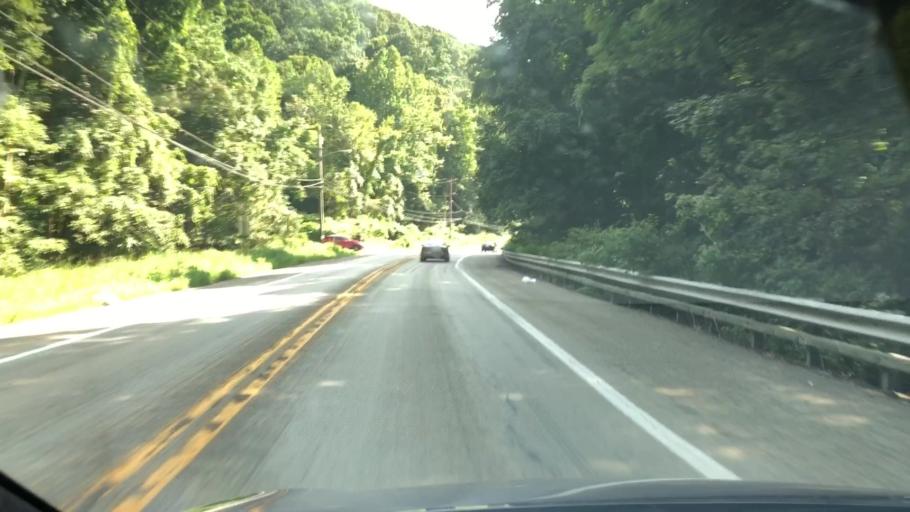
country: US
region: Pennsylvania
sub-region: Allegheny County
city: Pitcairn
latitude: 40.4055
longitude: -79.7619
